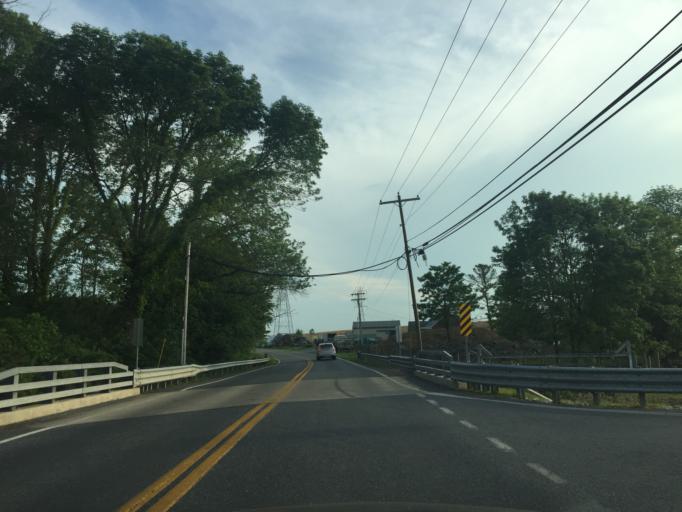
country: US
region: Maryland
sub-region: Frederick County
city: Adamstown
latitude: 39.3303
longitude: -77.4880
